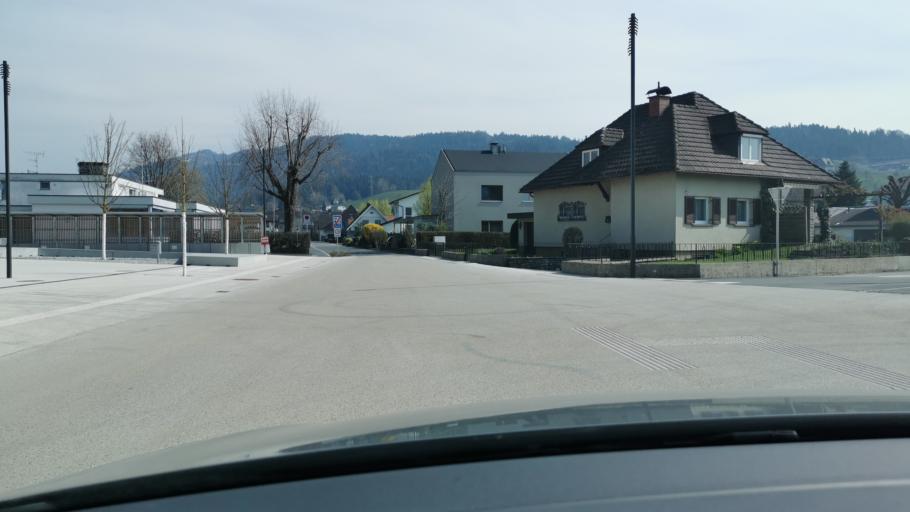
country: AT
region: Vorarlberg
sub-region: Politischer Bezirk Bregenz
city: Wolfurt
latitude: 47.4760
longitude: 9.7476
